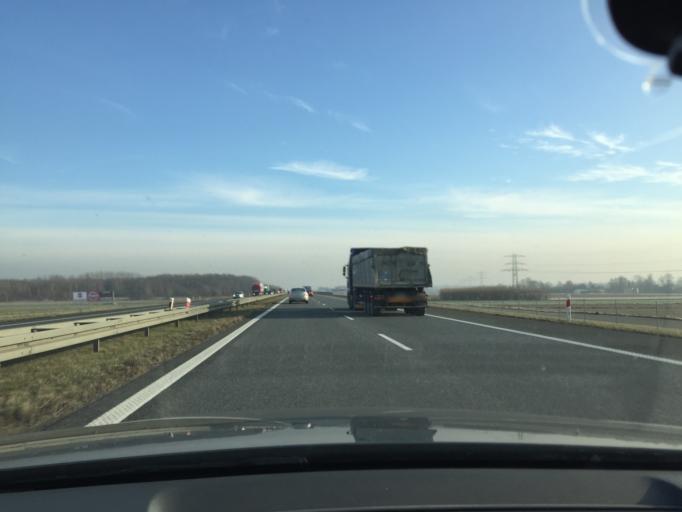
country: PL
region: Silesian Voivodeship
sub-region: Powiat gliwicki
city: Zernica
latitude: 50.2650
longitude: 18.6033
